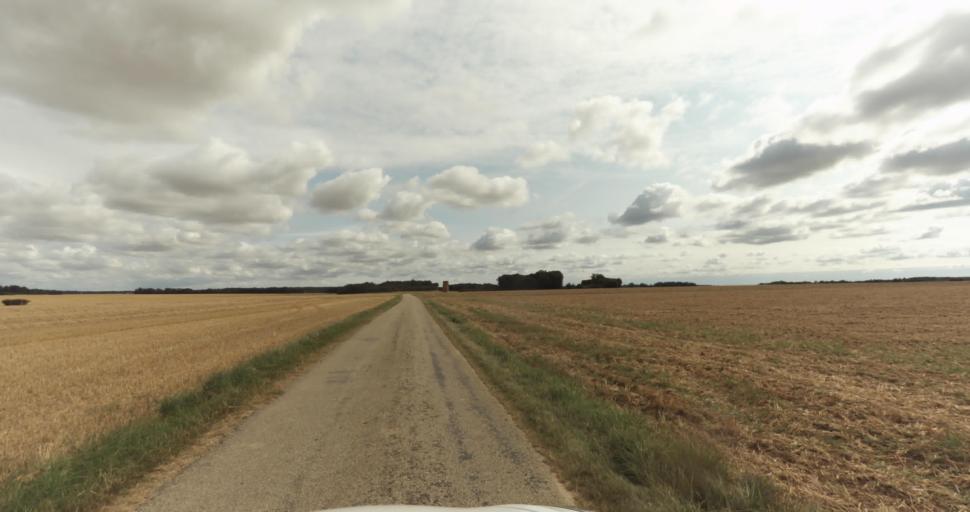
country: FR
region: Haute-Normandie
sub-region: Departement de l'Eure
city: Tillieres-sur-Avre
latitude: 48.7825
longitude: 1.0769
